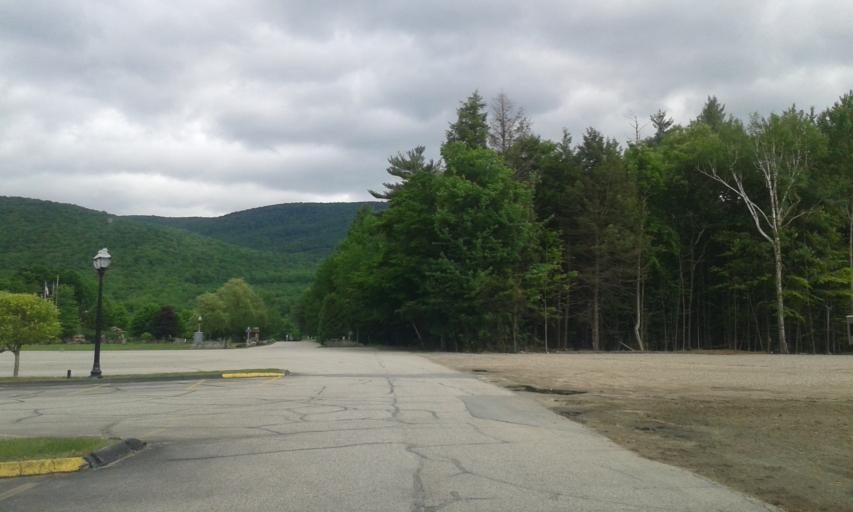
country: US
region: New Hampshire
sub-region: Grafton County
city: Woodstock
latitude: 44.0399
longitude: -71.6799
